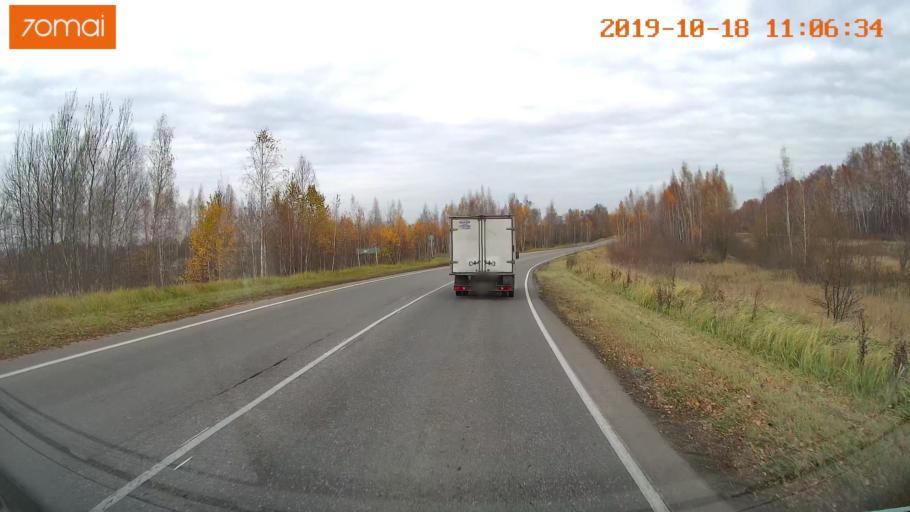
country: RU
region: Tula
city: Kimovsk
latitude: 53.9191
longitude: 38.5351
